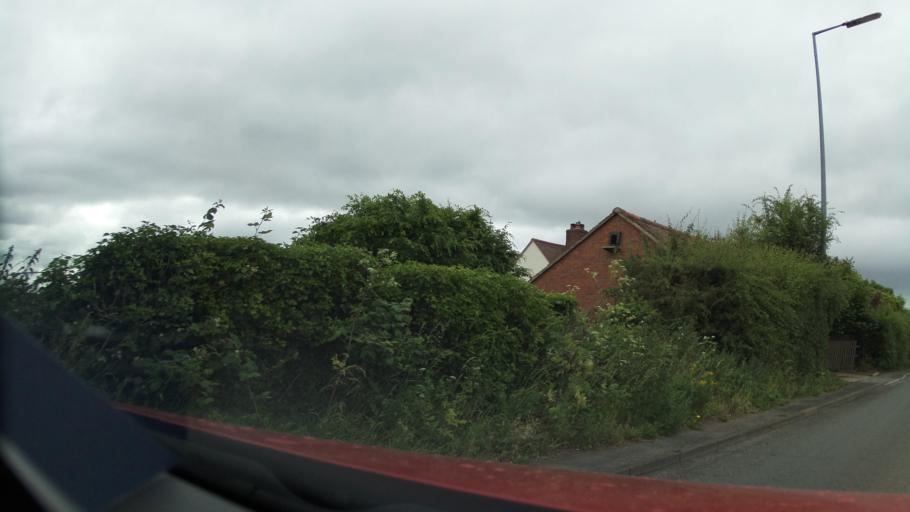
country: GB
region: England
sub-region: Staffordshire
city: Burton upon Trent
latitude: 52.8353
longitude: -1.6547
